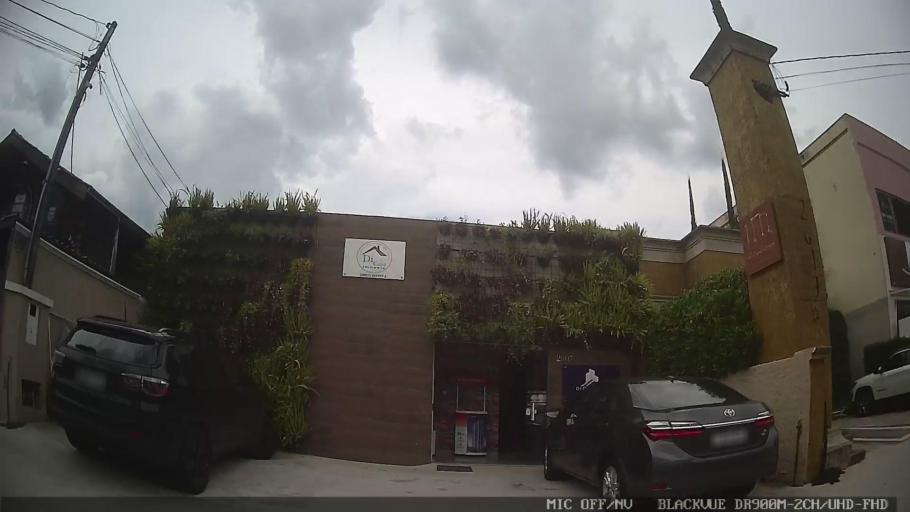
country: BR
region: Sao Paulo
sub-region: Atibaia
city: Atibaia
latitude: -23.1312
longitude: -46.5542
